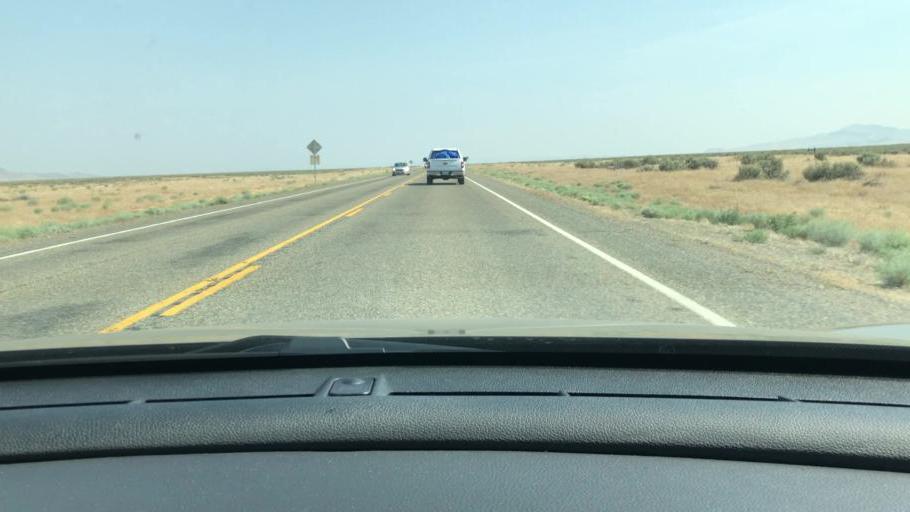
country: US
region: Nevada
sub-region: Humboldt County
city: Winnemucca
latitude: 41.7301
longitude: -117.7662
